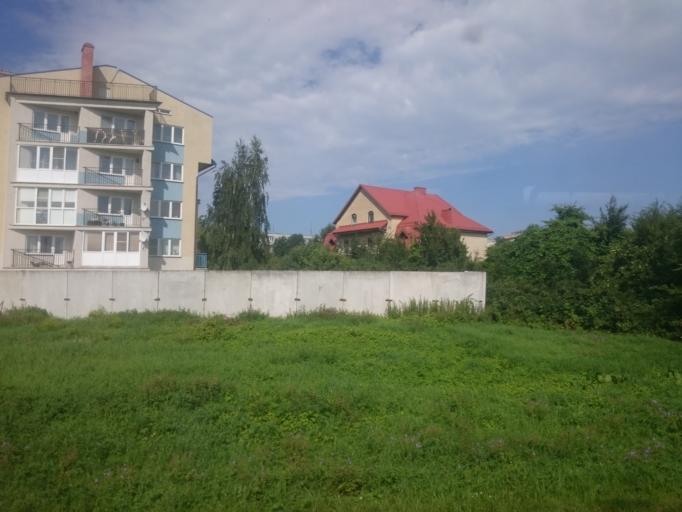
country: RU
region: Kaliningrad
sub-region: Zelenogradskiy Rayon
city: Zelenogradsk
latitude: 54.9538
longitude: 20.4719
